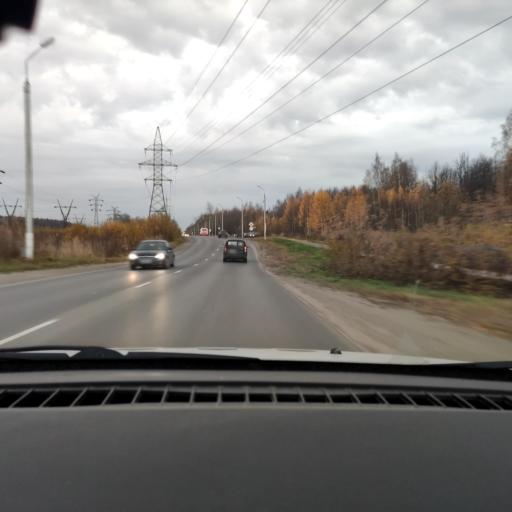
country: RU
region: Perm
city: Perm
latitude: 58.0977
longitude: 56.3955
